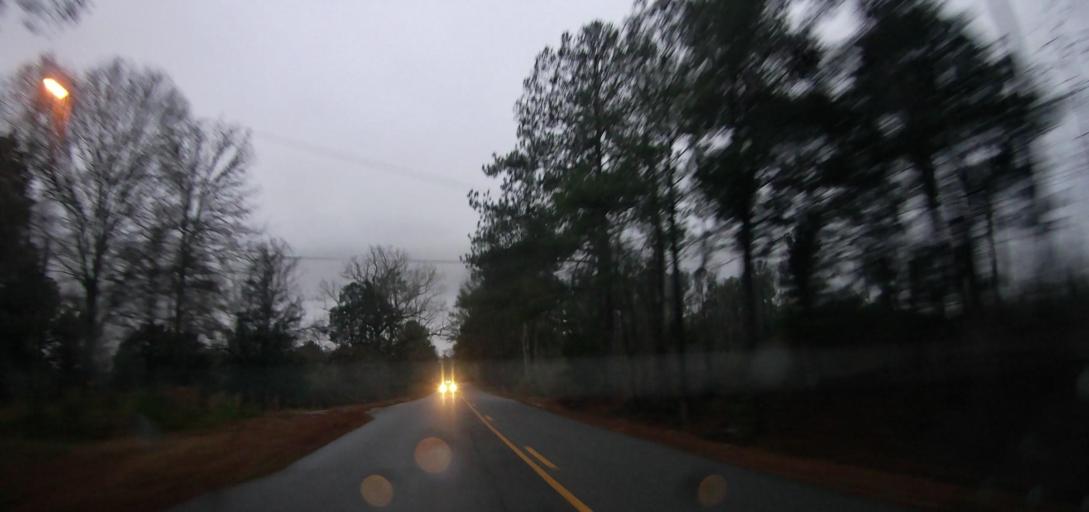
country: US
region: Alabama
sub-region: Tuscaloosa County
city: Vance
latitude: 33.1343
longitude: -87.2296
